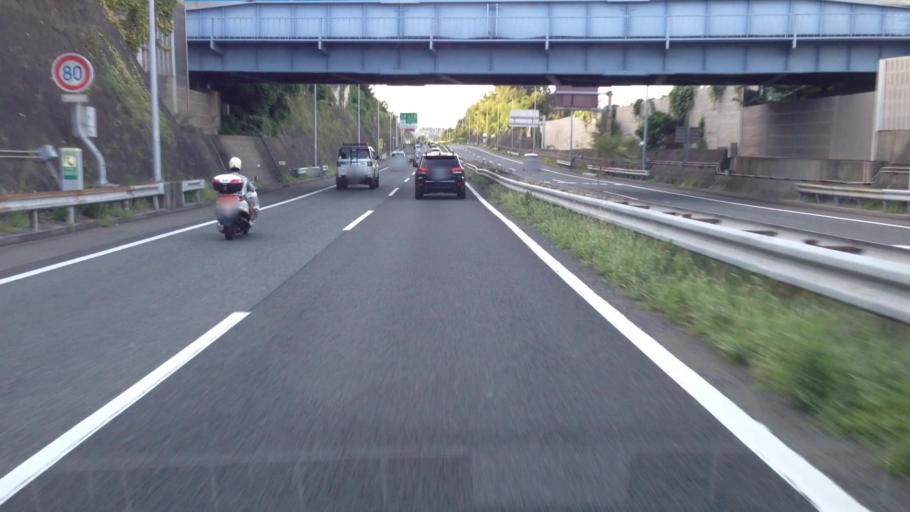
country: JP
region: Kanagawa
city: Kamakura
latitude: 35.3757
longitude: 139.5889
